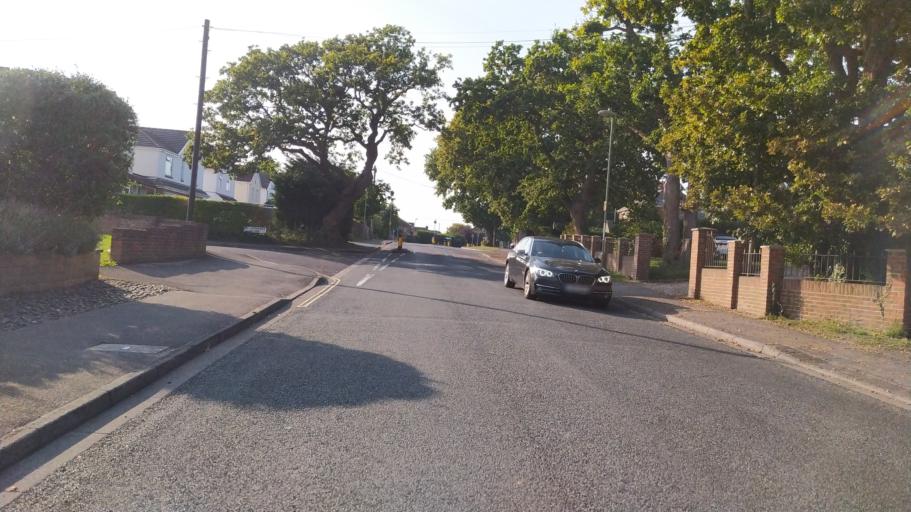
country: GB
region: England
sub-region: Hampshire
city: Botley
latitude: 50.8631
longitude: -1.2437
